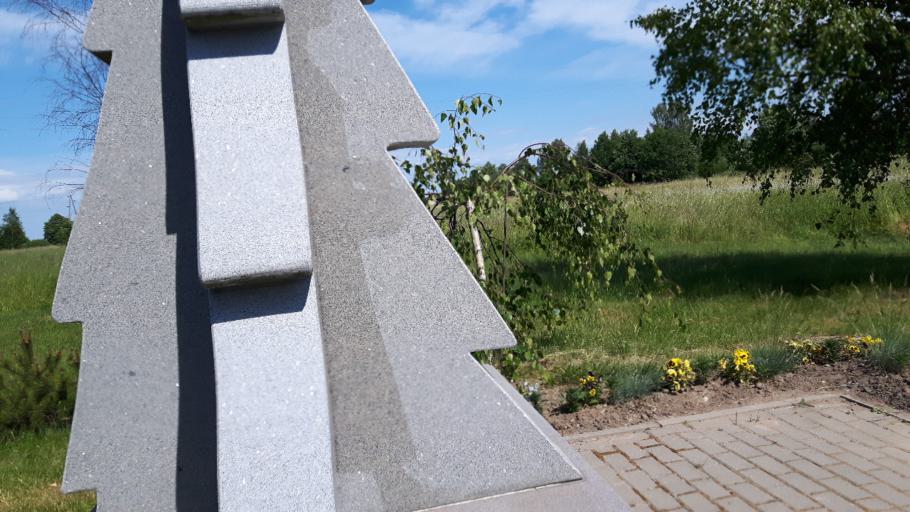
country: LV
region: Aizpute
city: Aizpute
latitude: 56.7972
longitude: 21.6698
